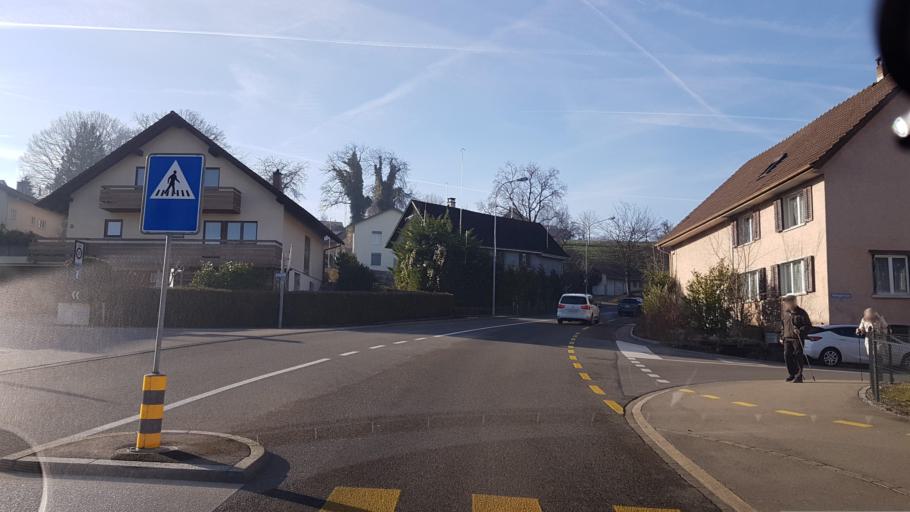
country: CH
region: Aargau
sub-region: Bezirk Muri
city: Muri
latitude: 47.2715
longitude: 8.3331
